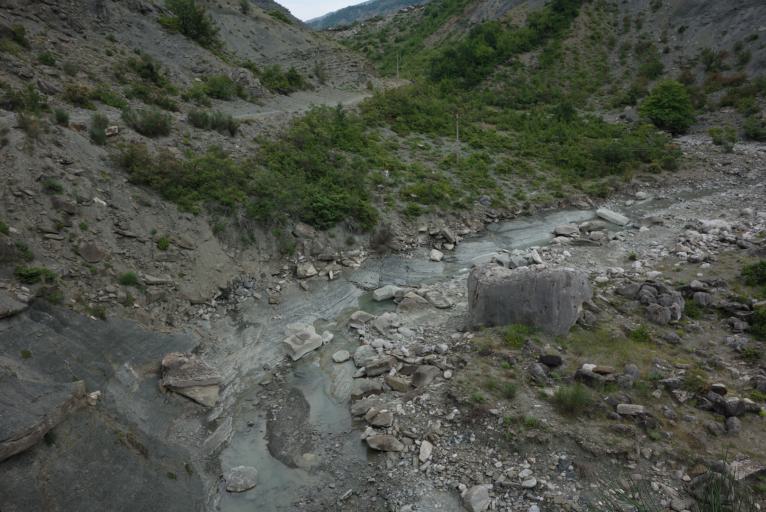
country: AL
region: Gjirokaster
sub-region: Rrethi i Permetit
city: Frasher
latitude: 40.3859
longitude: 20.3748
